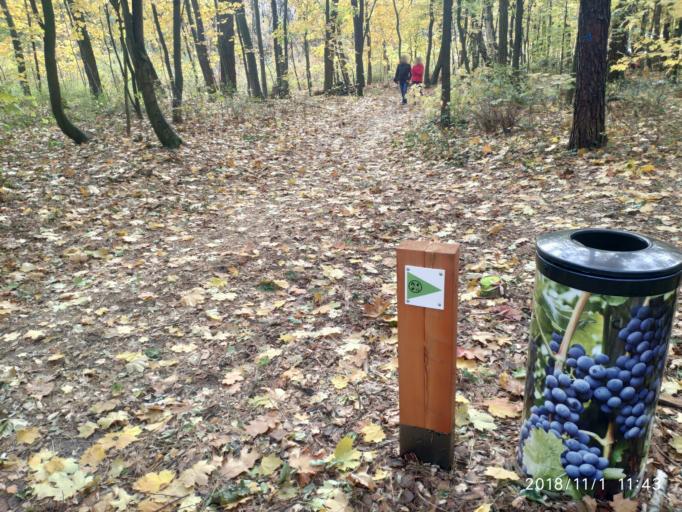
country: PL
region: Lubusz
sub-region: Zielona Gora
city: Zielona Gora
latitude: 51.9302
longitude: 15.5321
